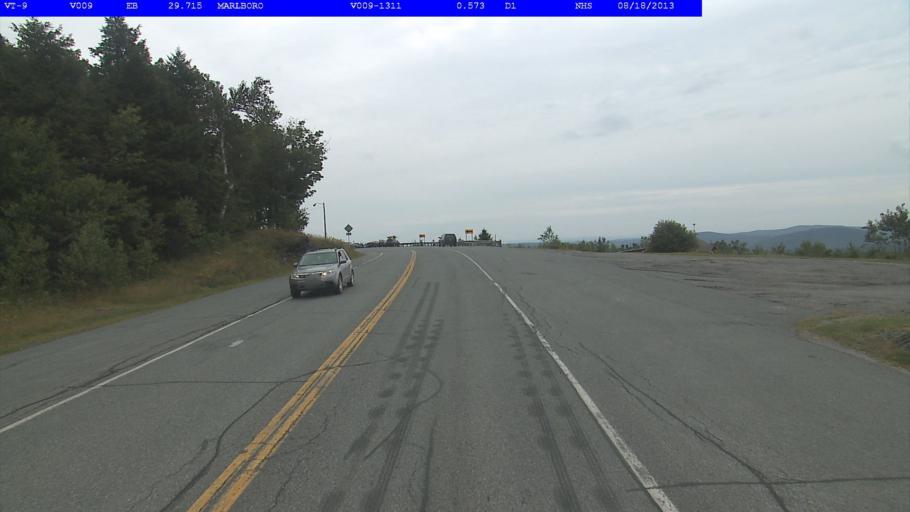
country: US
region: Vermont
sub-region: Windham County
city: Dover
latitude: 42.8530
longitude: -72.7956
